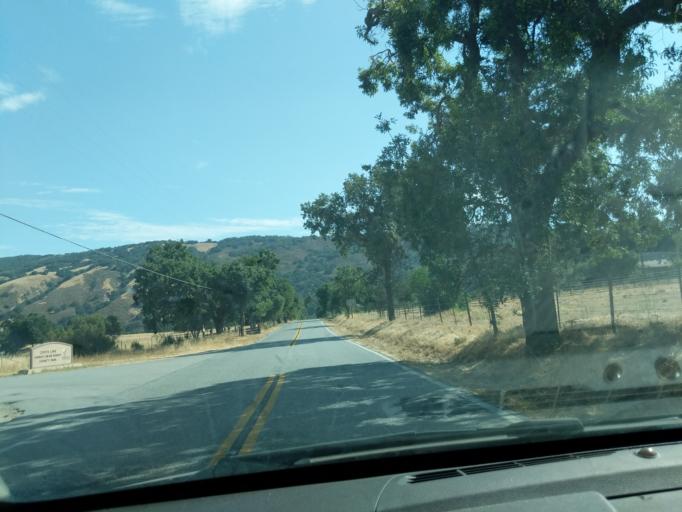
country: US
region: California
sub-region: Santa Clara County
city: Gilroy
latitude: 37.0697
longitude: -121.5204
